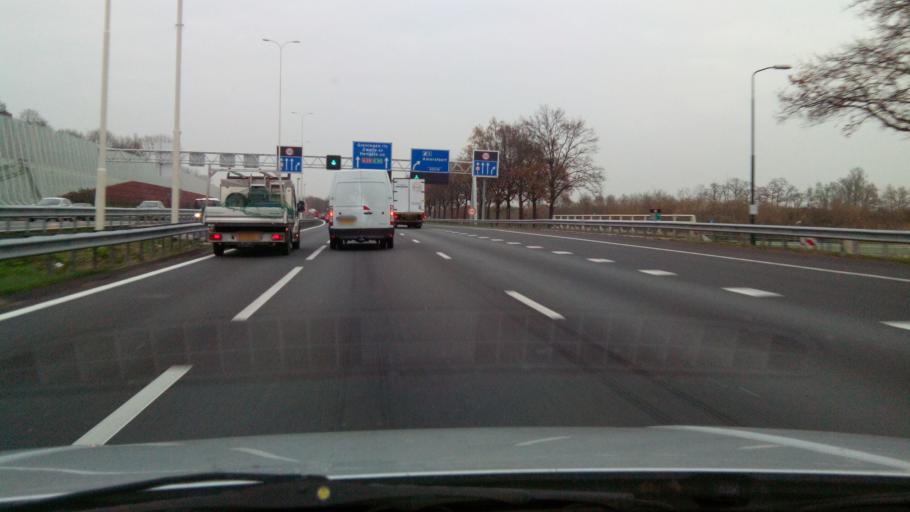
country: NL
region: Utrecht
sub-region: Gemeente Amersfoort
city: Randenbroek
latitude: 52.1469
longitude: 5.4125
